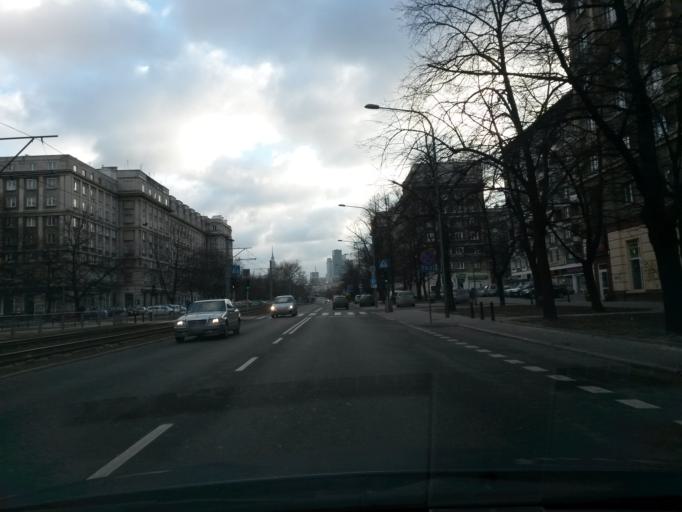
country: PL
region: Masovian Voivodeship
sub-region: Warszawa
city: Wola
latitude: 52.2514
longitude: 20.9982
